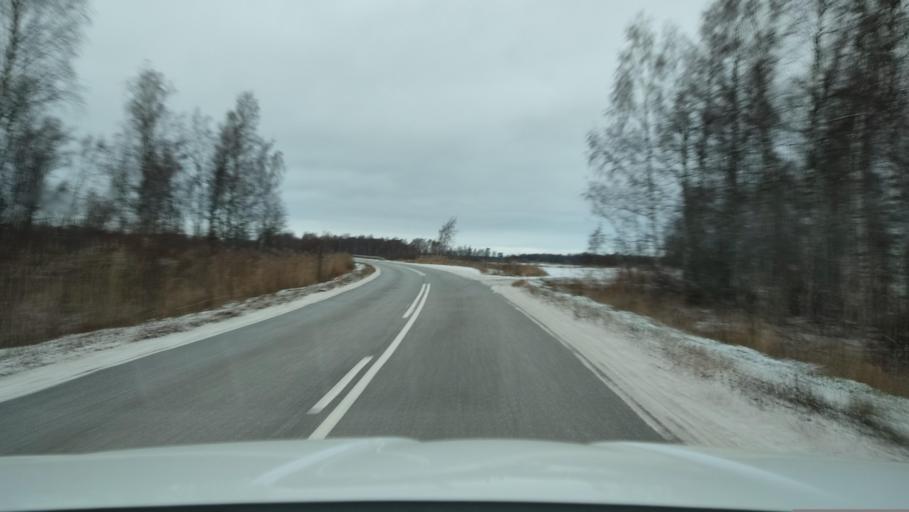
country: FI
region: Ostrobothnia
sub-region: Vaasa
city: Replot
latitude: 63.2802
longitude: 21.3406
